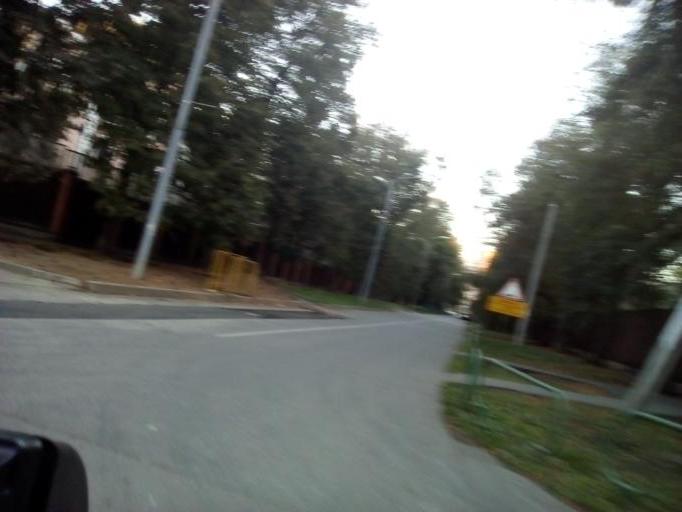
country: RU
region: Moscow
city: Sokol
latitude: 55.8023
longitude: 37.5023
